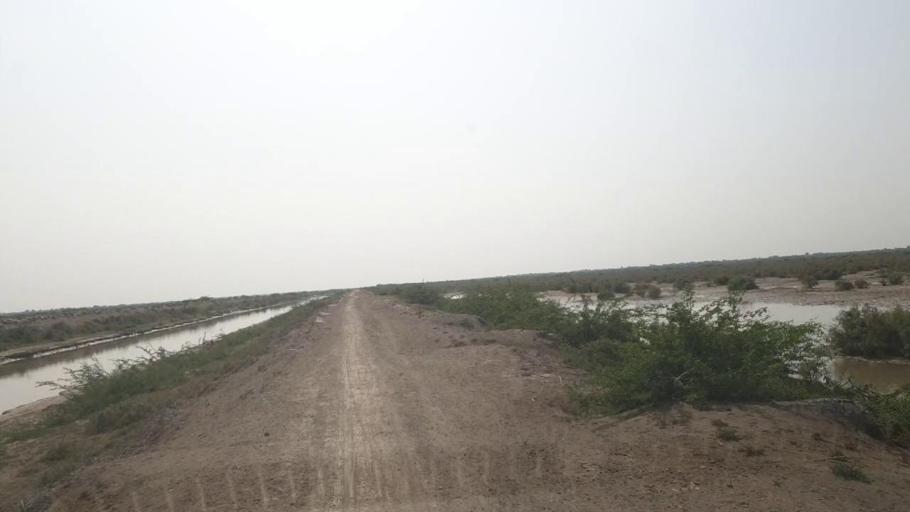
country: PK
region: Sindh
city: Kadhan
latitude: 24.3790
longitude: 68.8970
